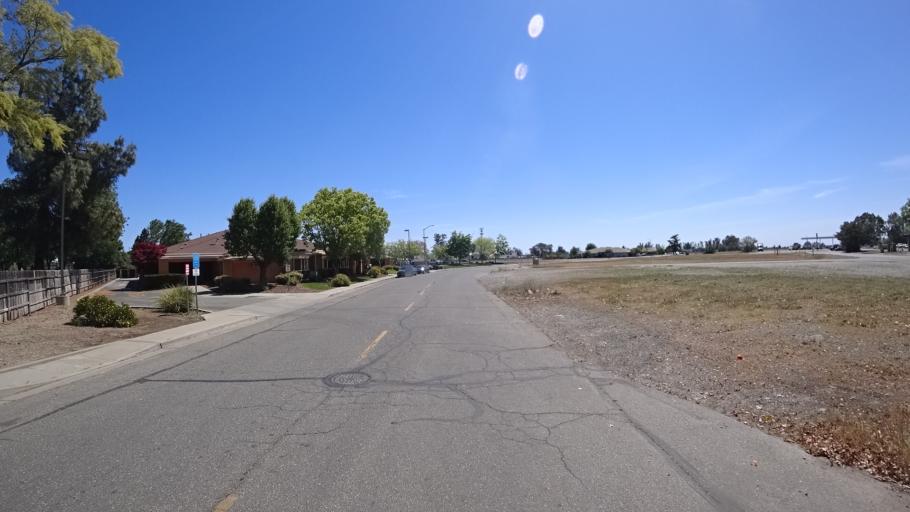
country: US
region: California
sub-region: Glenn County
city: Orland
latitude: 39.7420
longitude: -122.2021
